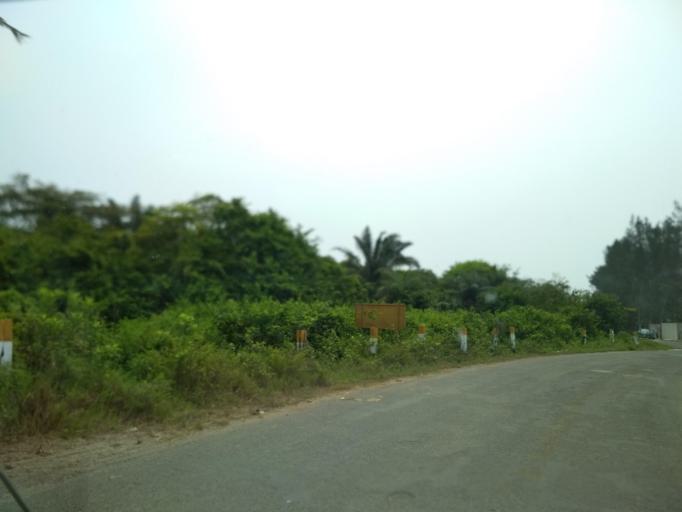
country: MX
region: Veracruz
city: Anton Lizardo
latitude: 19.0395
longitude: -95.9732
